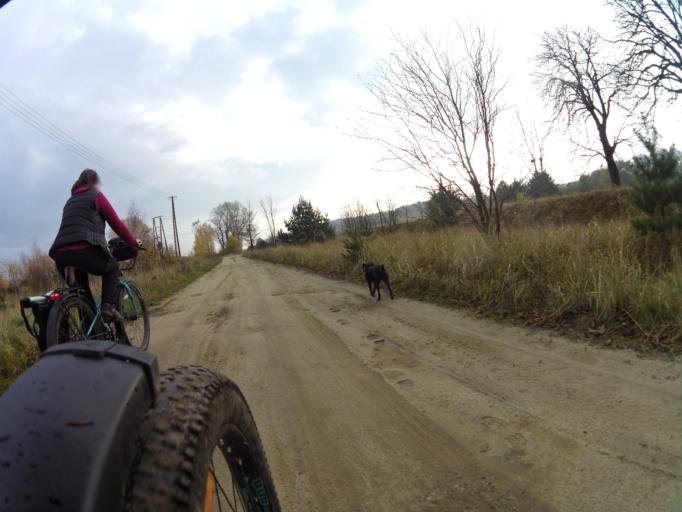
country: PL
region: Pomeranian Voivodeship
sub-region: Powiat wejherowski
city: Gniewino
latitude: 54.7100
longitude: 18.0979
